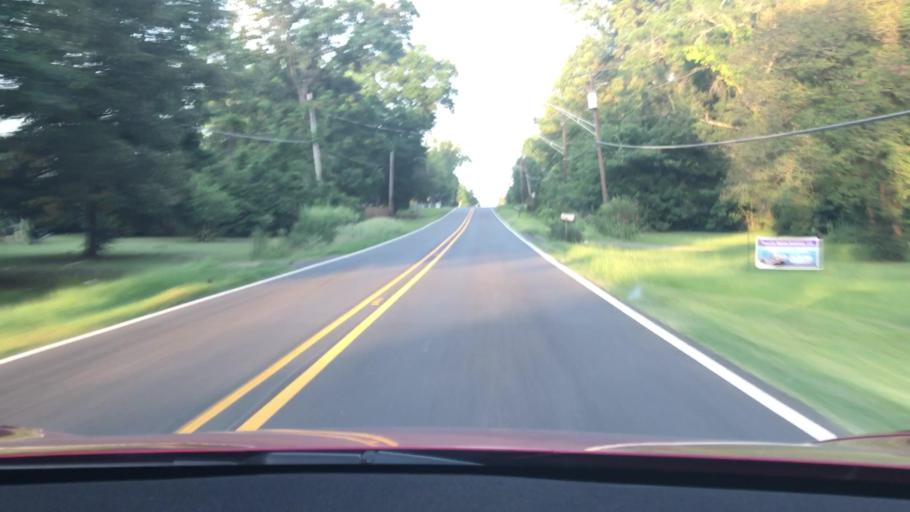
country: US
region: Louisiana
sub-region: De Soto Parish
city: Stonewall
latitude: 32.3910
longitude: -93.7618
